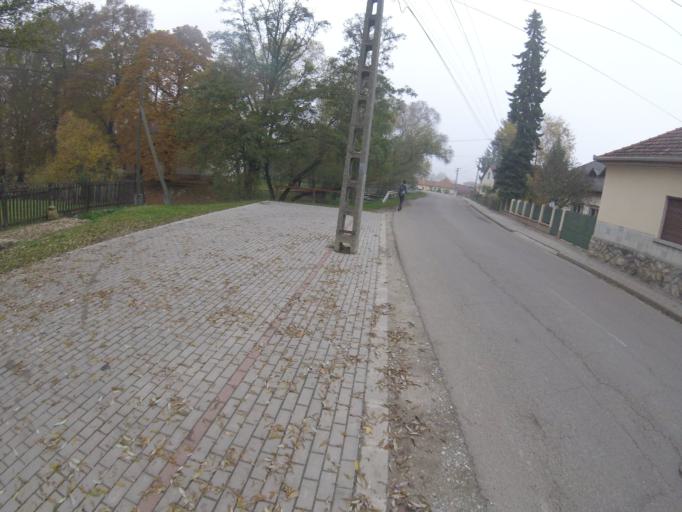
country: HU
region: Heves
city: Szilvasvarad
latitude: 48.1761
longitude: 20.4865
